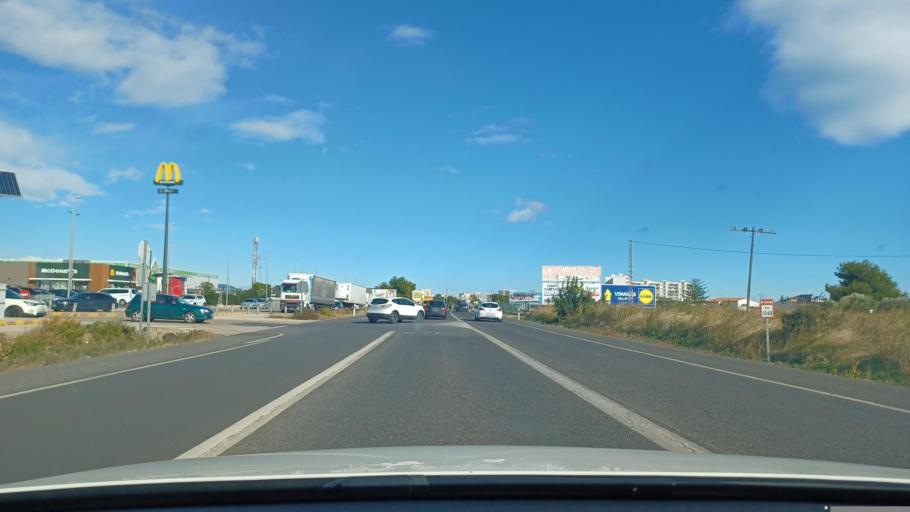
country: ES
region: Valencia
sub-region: Provincia de Castello
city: Vinaros
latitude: 40.4542
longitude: 0.4533
